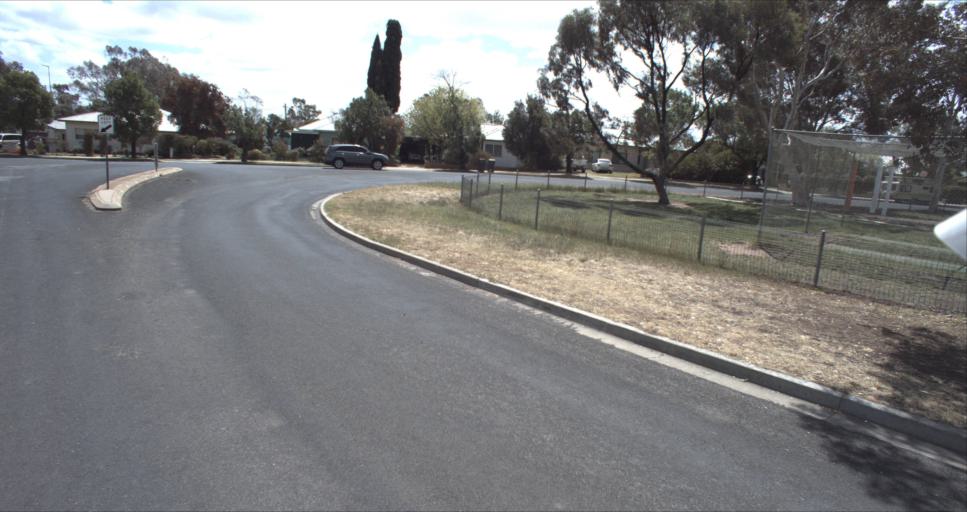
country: AU
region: New South Wales
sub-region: Leeton
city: Leeton
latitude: -34.5615
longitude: 146.3946
